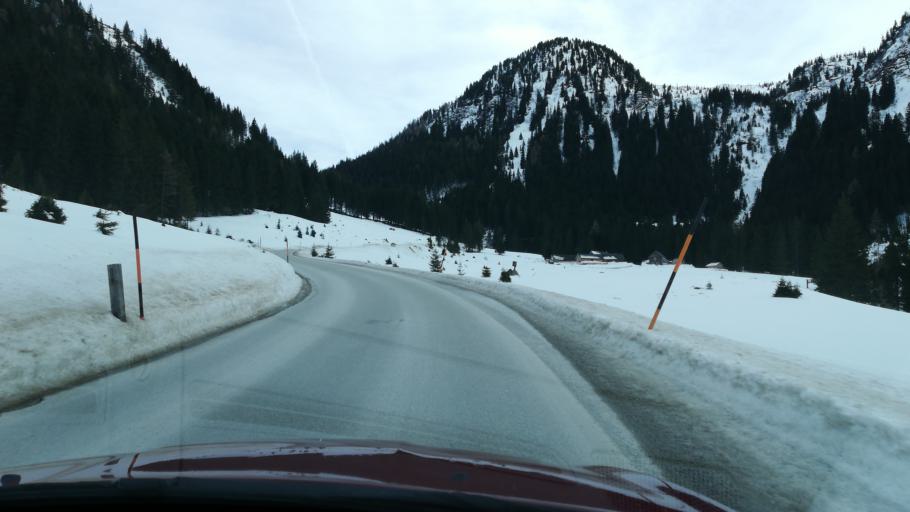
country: AT
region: Styria
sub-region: Politischer Bezirk Liezen
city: Donnersbach
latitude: 47.4147
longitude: 14.1765
